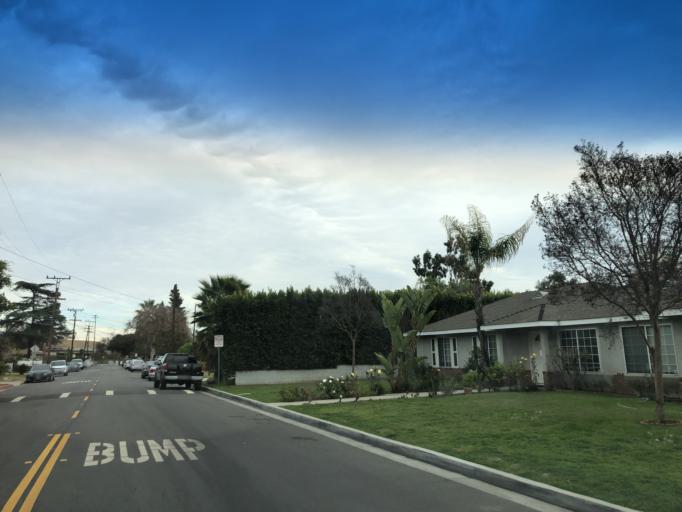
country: US
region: California
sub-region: Los Angeles County
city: Monrovia
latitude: 34.1359
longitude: -118.0126
